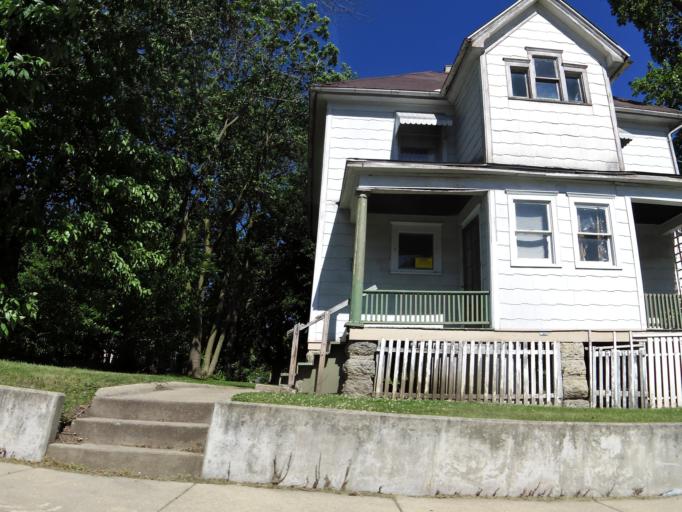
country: US
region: Illinois
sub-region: Winnebago County
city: Rockford
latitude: 42.2623
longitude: -89.0719
